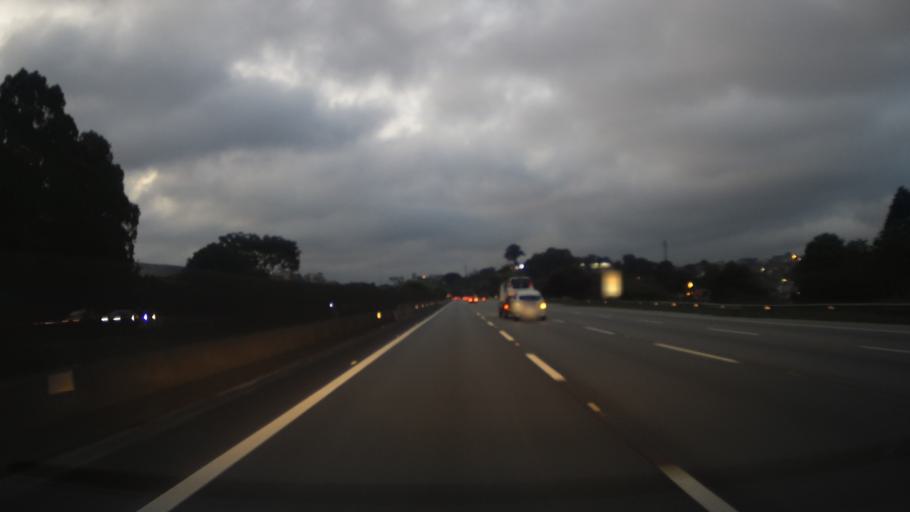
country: BR
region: Sao Paulo
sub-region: Diadema
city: Diadema
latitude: -23.6862
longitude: -46.6065
